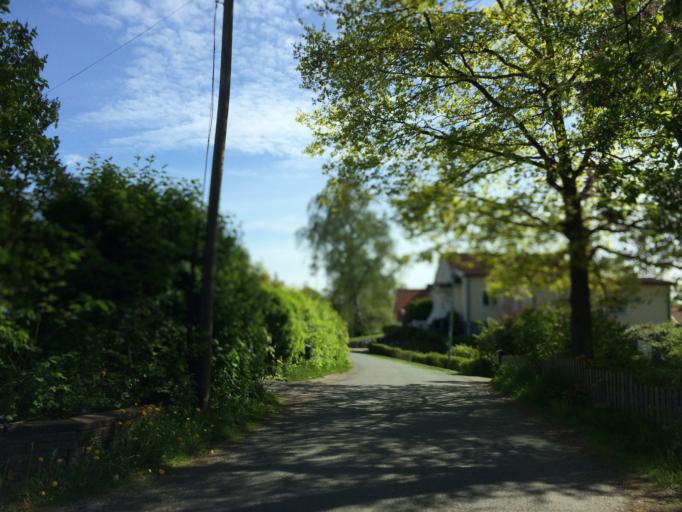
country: SE
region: Stockholm
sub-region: Sollentuna Kommun
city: Sollentuna
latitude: 59.4589
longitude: 17.9177
